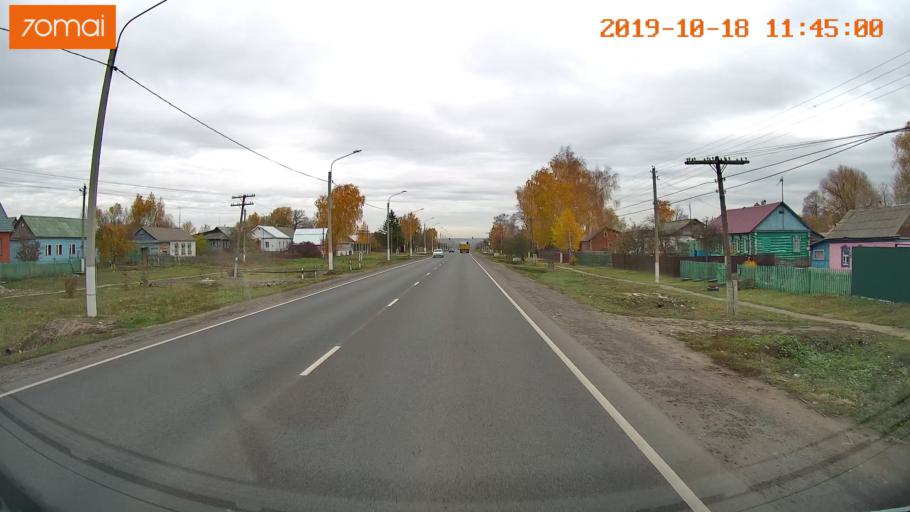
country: RU
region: Rjazan
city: Mikhaylov
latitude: 54.2069
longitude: 38.9648
